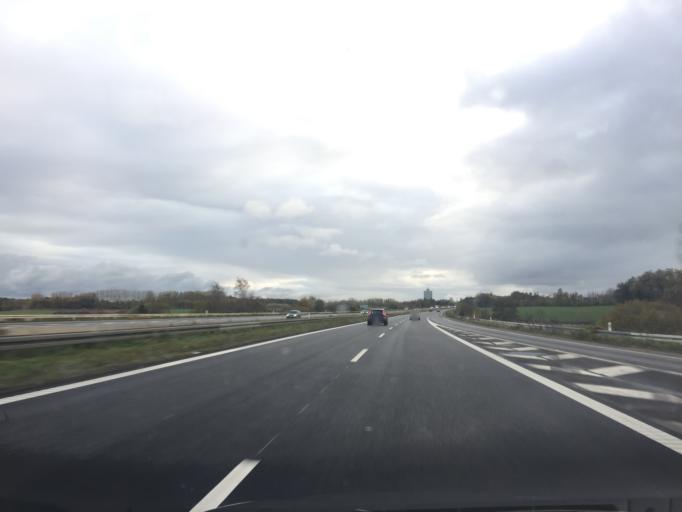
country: DK
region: Capital Region
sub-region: Fredensborg Kommune
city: Niva
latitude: 55.9342
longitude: 12.4793
